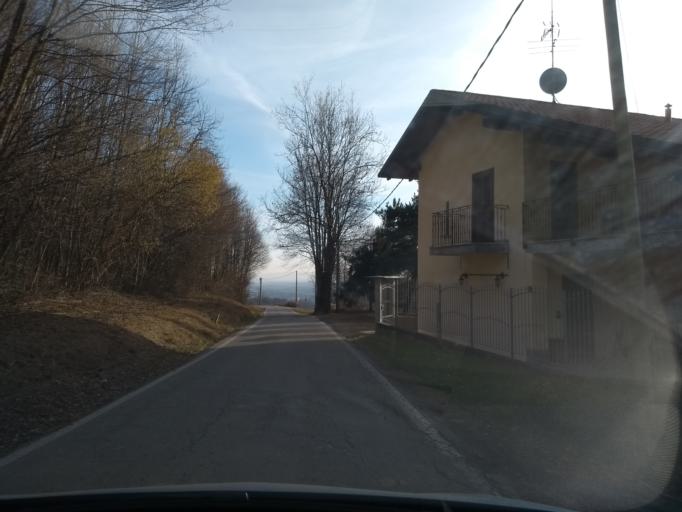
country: IT
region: Piedmont
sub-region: Provincia di Torino
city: Lanzo Torinese
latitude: 45.2932
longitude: 7.4939
